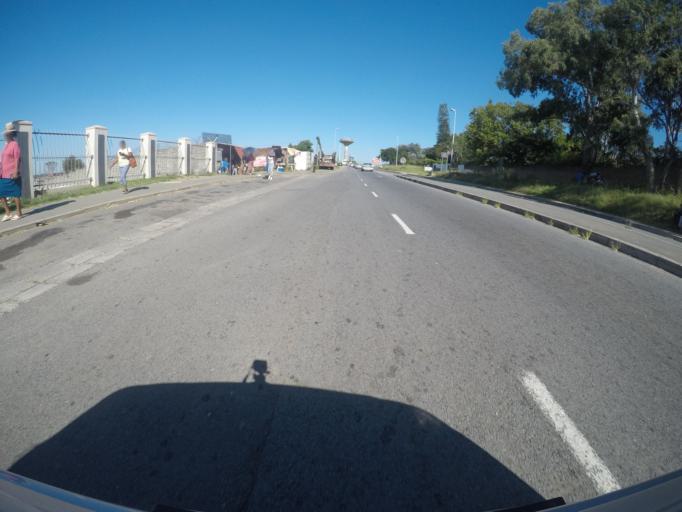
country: ZA
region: Eastern Cape
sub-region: Buffalo City Metropolitan Municipality
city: East London
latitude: -32.9508
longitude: 27.9284
